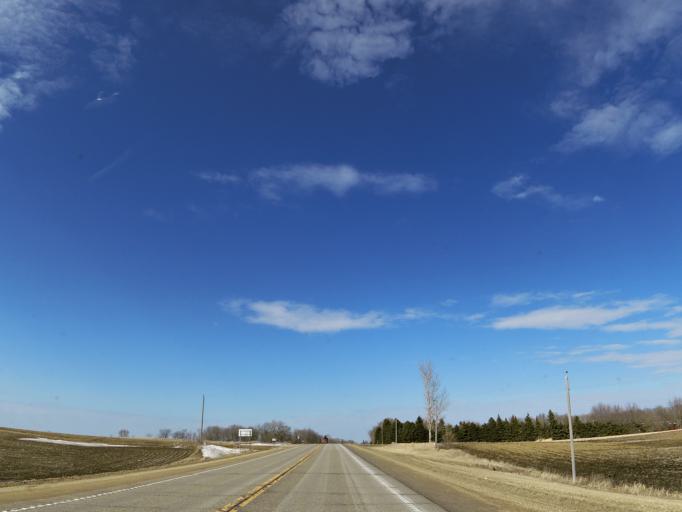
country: US
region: Minnesota
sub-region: Waseca County
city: Waseca
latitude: 44.1554
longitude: -93.5073
